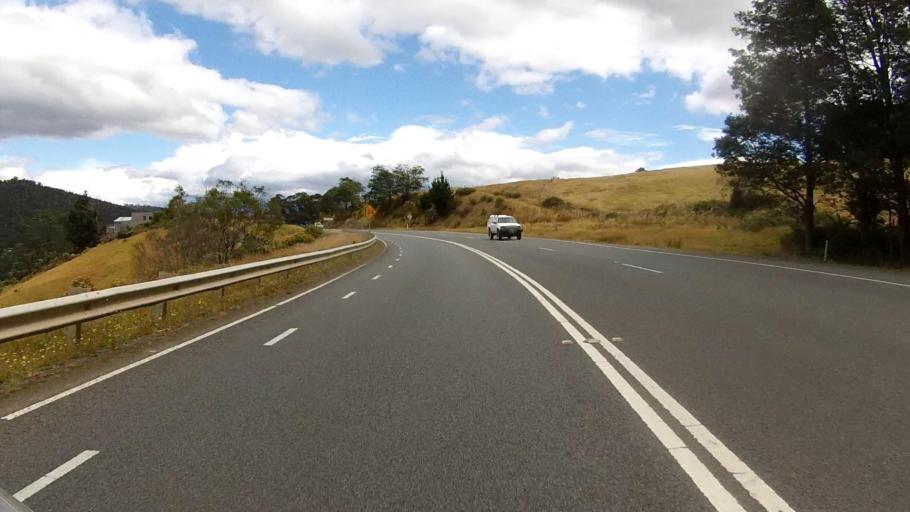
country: AU
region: Tasmania
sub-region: Kingborough
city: Margate
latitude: -42.9767
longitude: 147.1569
